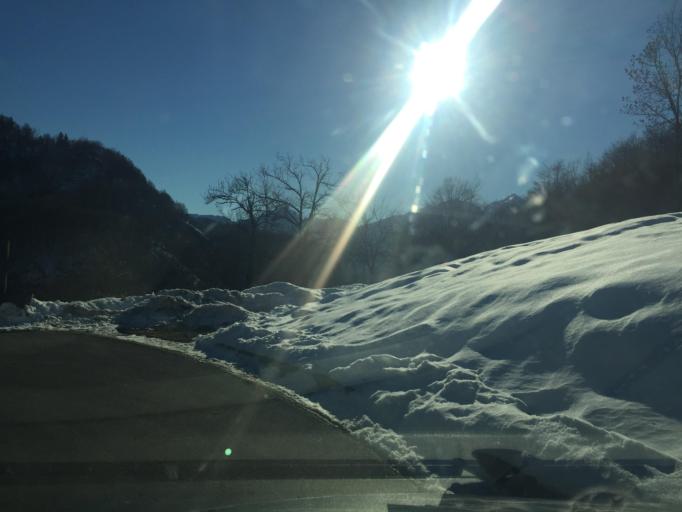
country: IT
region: Friuli Venezia Giulia
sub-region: Provincia di Udine
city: Lauco
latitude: 46.4380
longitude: 12.9684
